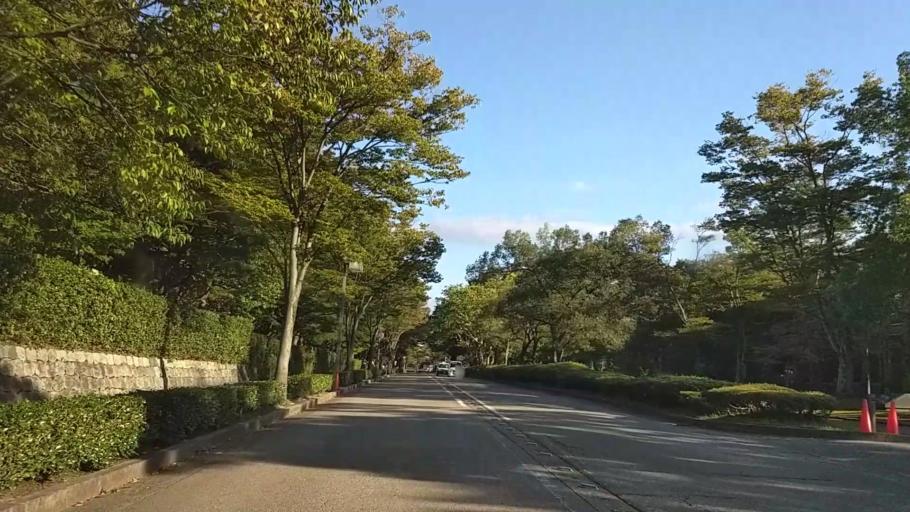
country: JP
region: Ishikawa
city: Kanazawa-shi
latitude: 36.5597
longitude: 136.6629
